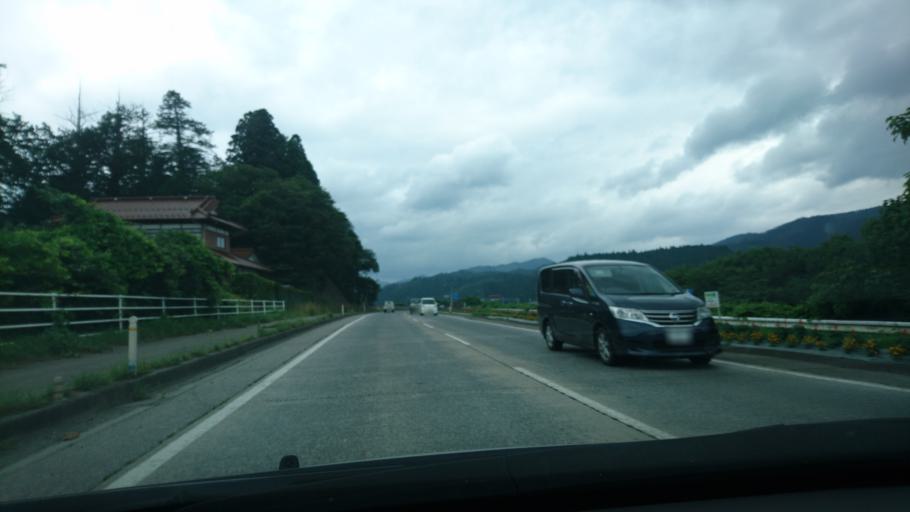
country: JP
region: Iwate
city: Ofunato
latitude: 38.9086
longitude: 141.5478
